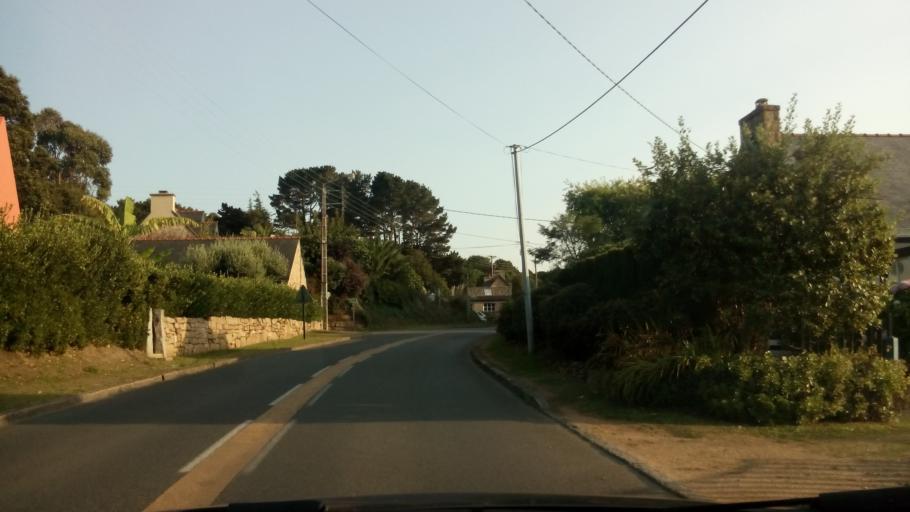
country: FR
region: Brittany
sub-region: Departement des Cotes-d'Armor
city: Trebeurden
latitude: 48.7893
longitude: -3.5514
